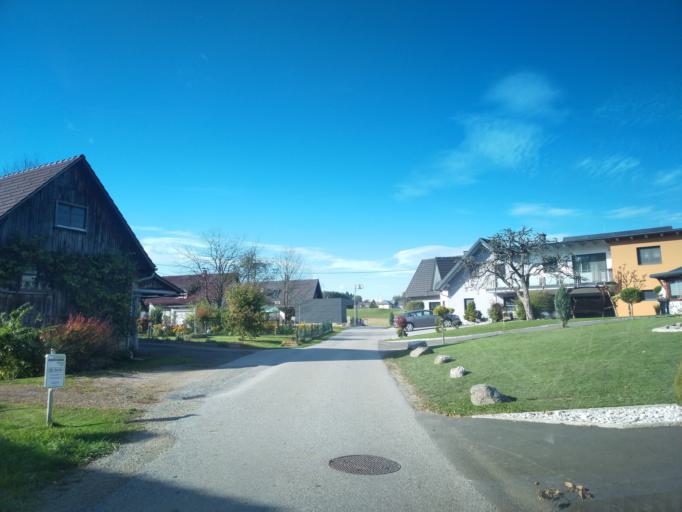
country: AT
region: Styria
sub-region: Politischer Bezirk Deutschlandsberg
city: Wies
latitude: 46.7244
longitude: 15.3012
